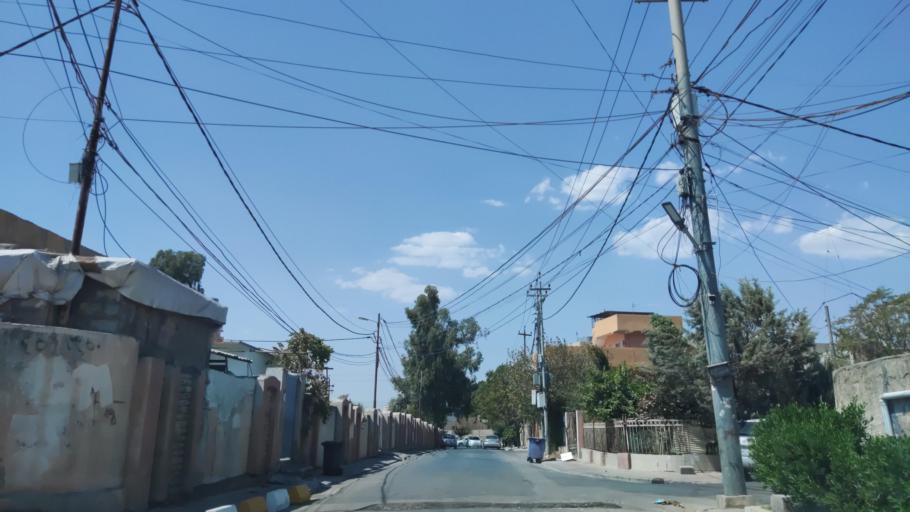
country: IQ
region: Arbil
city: Erbil
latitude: 36.1967
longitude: 44.0214
